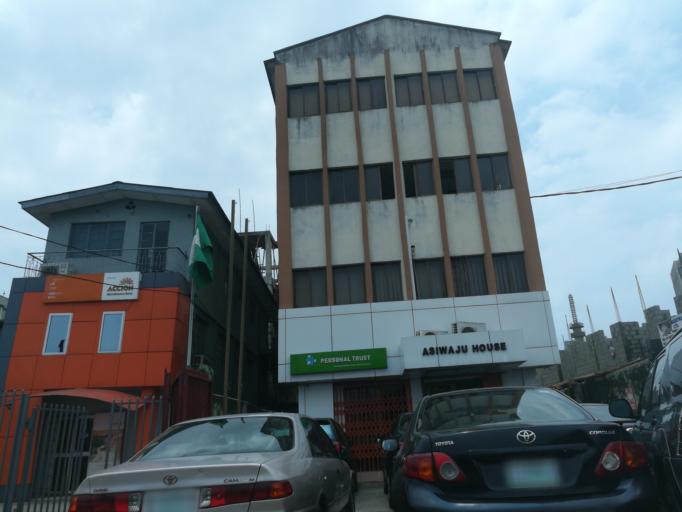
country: NG
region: Lagos
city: Lagos
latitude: 6.4511
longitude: 3.4009
